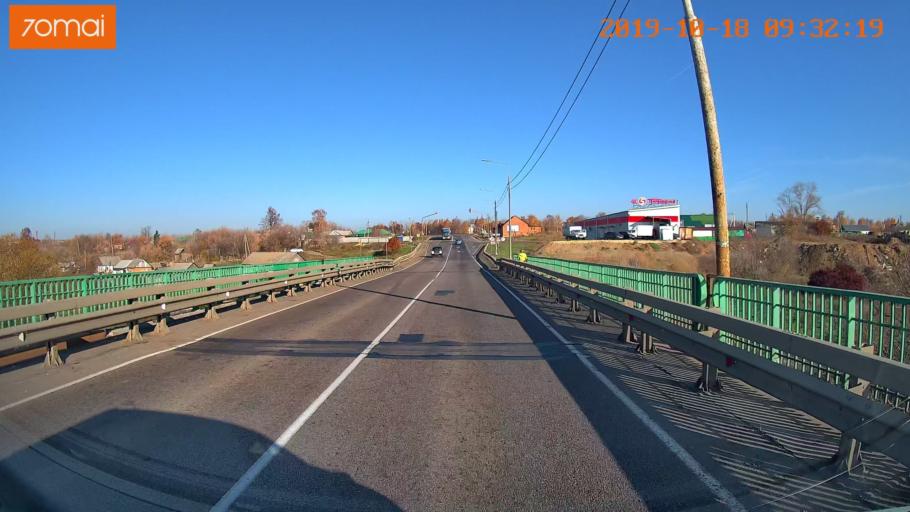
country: RU
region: Tula
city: Yefremov
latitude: 53.1595
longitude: 38.1556
